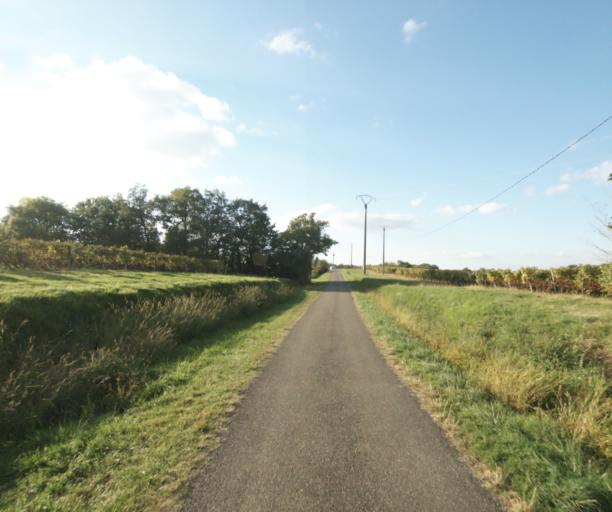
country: FR
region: Midi-Pyrenees
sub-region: Departement du Gers
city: Eauze
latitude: 43.7549
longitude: 0.0985
